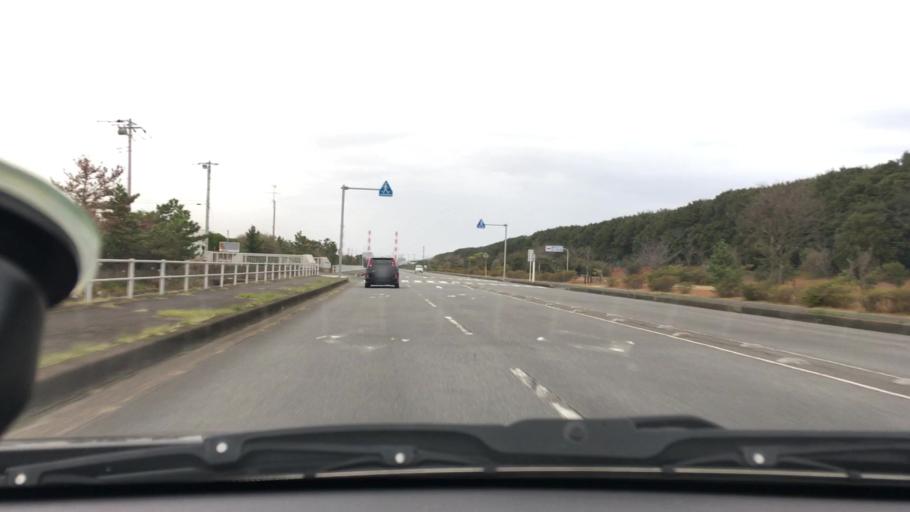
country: JP
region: Chiba
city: Omigawa
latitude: 35.8800
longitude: 140.7300
